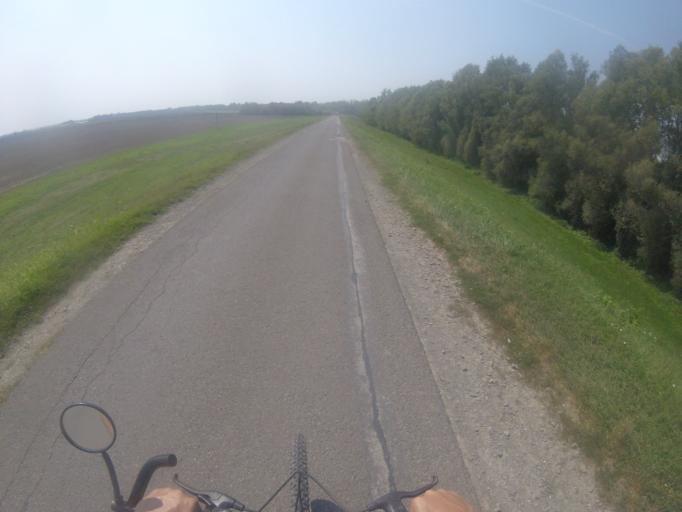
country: HU
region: Bacs-Kiskun
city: Baja
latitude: 46.2262
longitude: 18.9195
